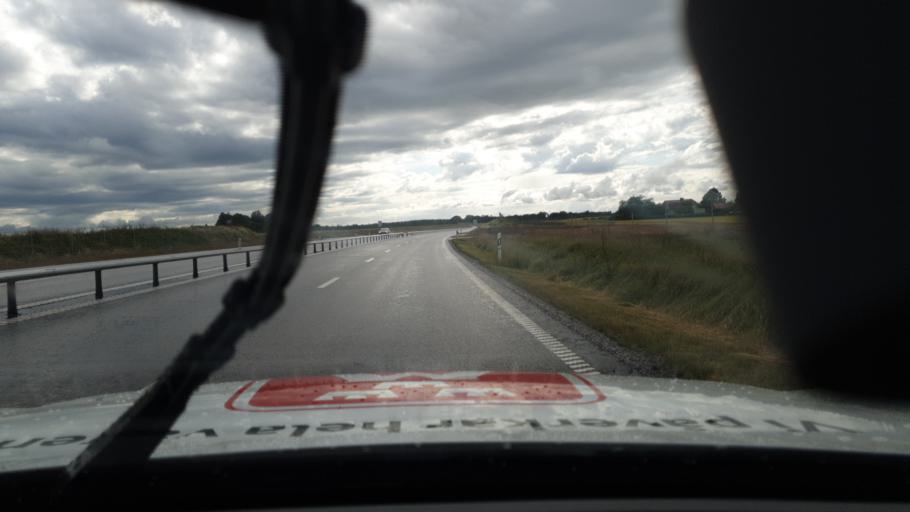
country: SE
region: Vaestra Goetaland
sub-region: Lidkopings Kommun
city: Vinninga
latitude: 58.4783
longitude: 13.2639
